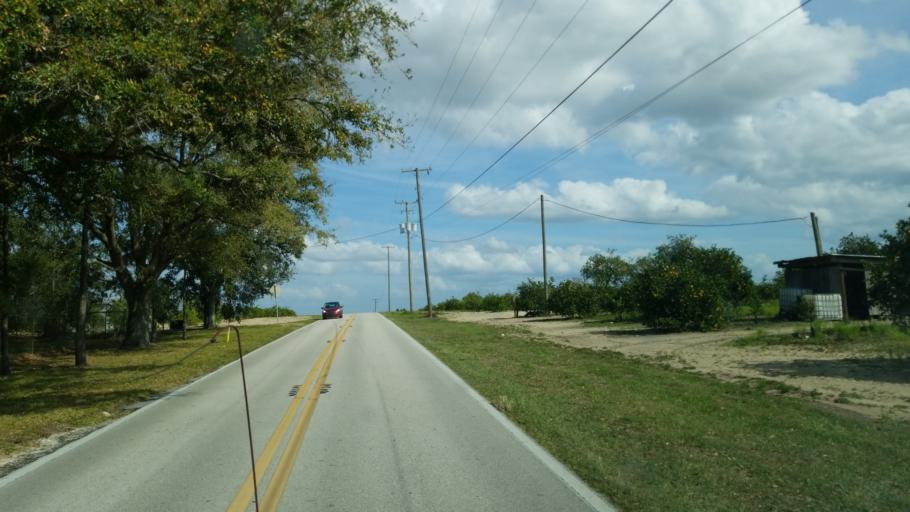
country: US
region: Florida
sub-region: Polk County
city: Dundee
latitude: 27.9773
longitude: -81.6016
